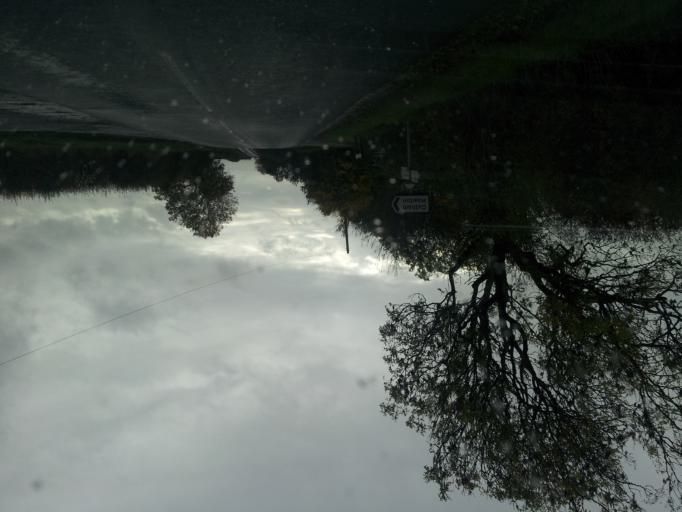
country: GB
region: England
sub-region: Lincolnshire
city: Long Bennington
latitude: 53.0111
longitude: -0.8041
